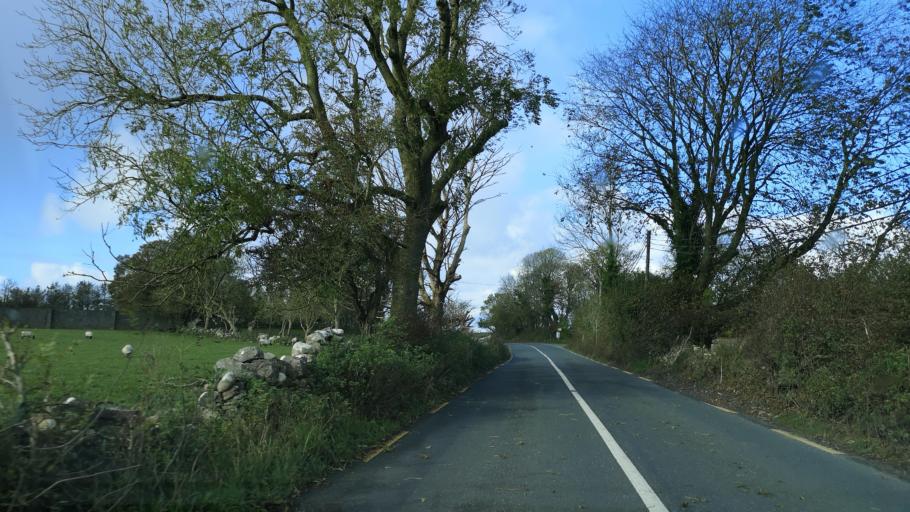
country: IE
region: Connaught
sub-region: Maigh Eo
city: Westport
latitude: 53.7760
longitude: -9.4022
